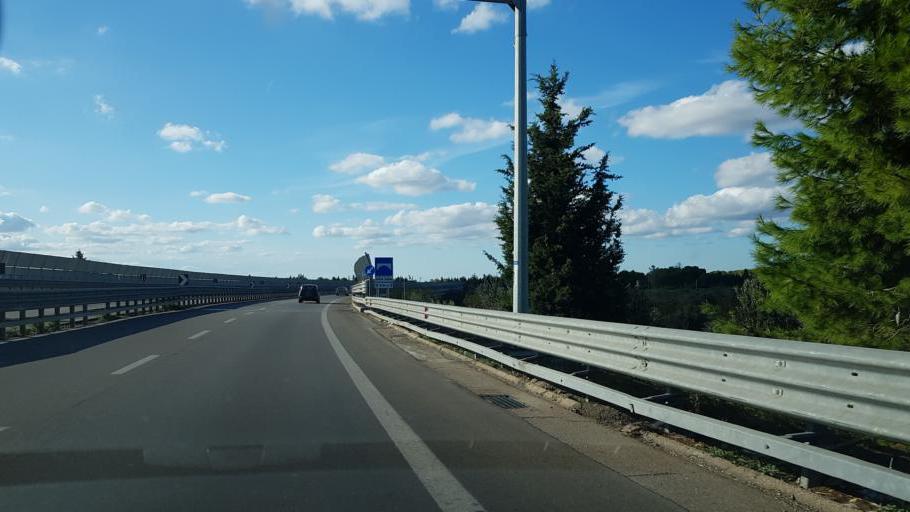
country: IT
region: Apulia
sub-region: Provincia di Lecce
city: Lequile
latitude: 40.3272
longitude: 18.1444
